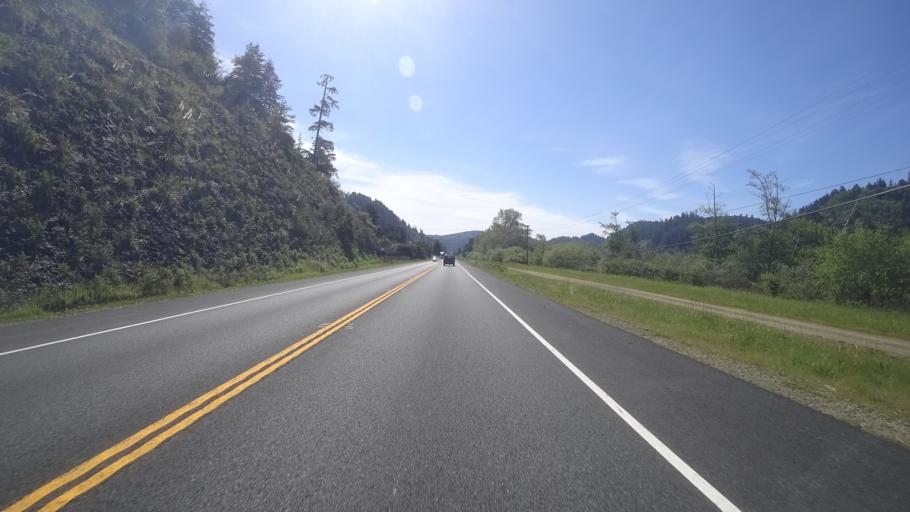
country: US
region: California
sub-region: Del Norte County
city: Bertsch-Oceanview
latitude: 41.5361
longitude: -124.0467
